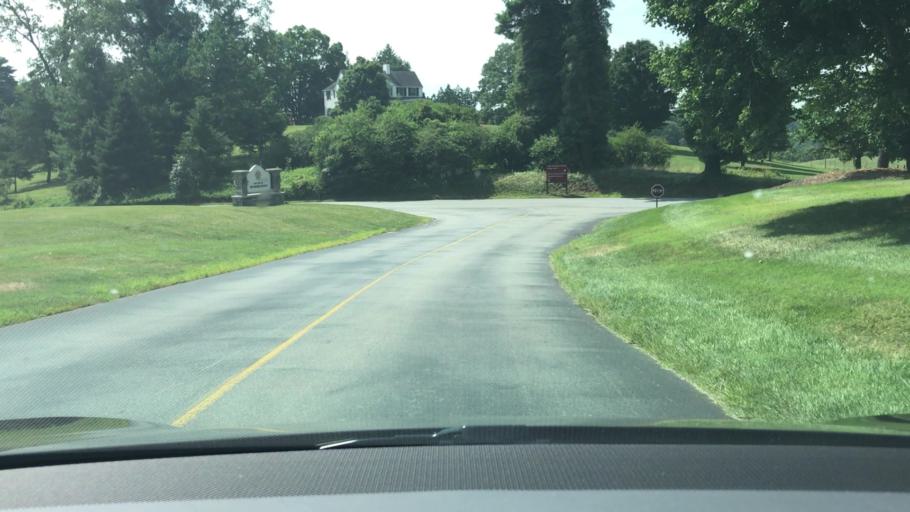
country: US
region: North Carolina
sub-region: Buncombe County
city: Asheville
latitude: 35.5574
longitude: -82.5772
